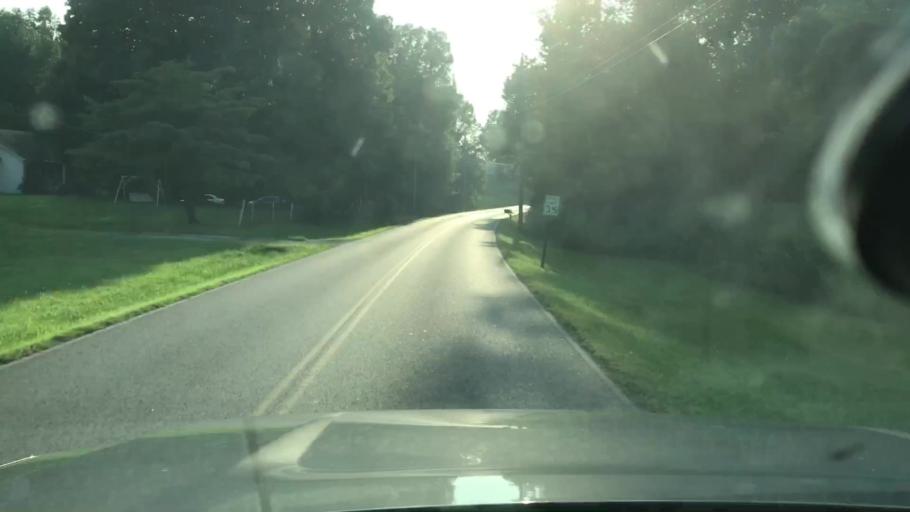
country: US
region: Tennessee
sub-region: Sumner County
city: Gallatin
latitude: 36.4820
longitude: -86.4419
